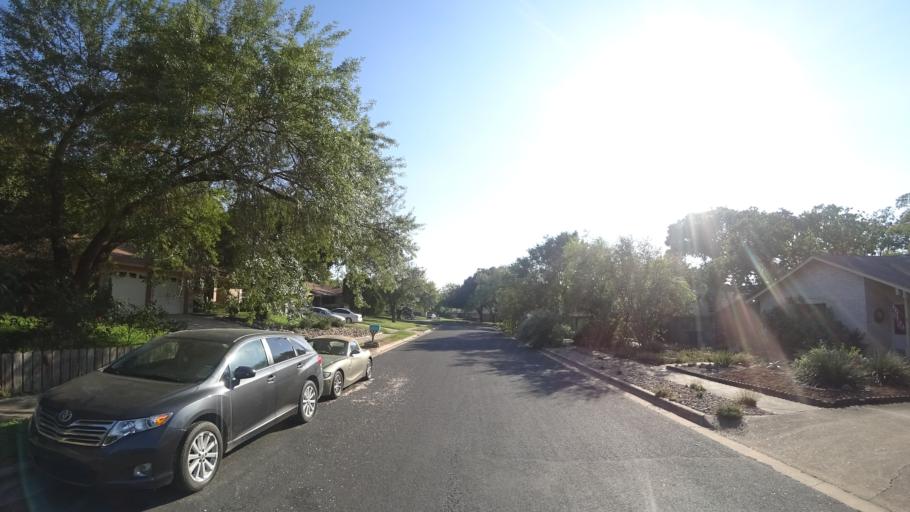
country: US
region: Texas
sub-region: Travis County
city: Wells Branch
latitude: 30.3558
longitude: -97.6746
